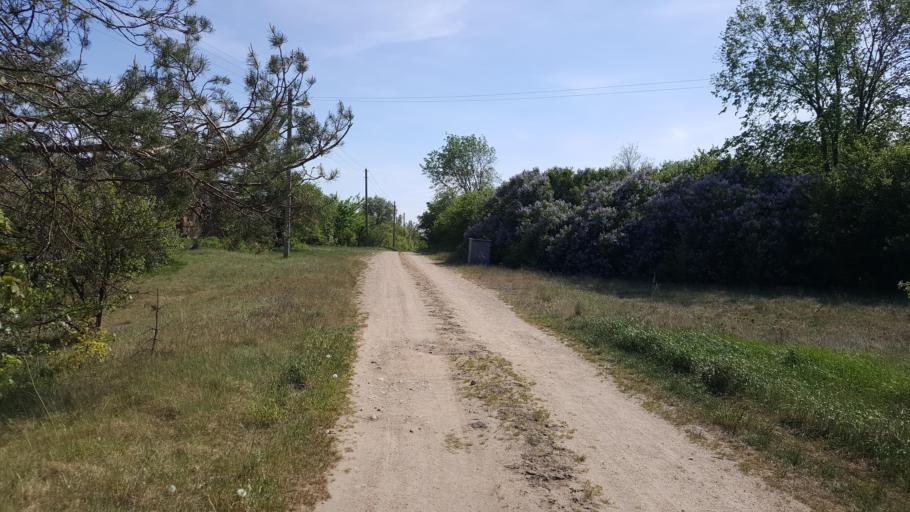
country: BY
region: Brest
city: Zhabinka
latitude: 52.3152
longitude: 24.0405
